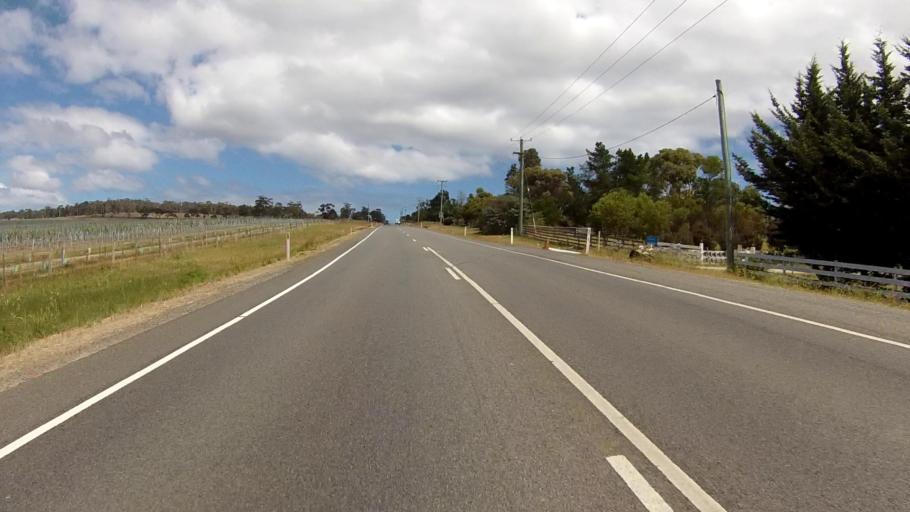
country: AU
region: Tasmania
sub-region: Sorell
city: Sorell
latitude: -42.8123
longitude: 147.6258
